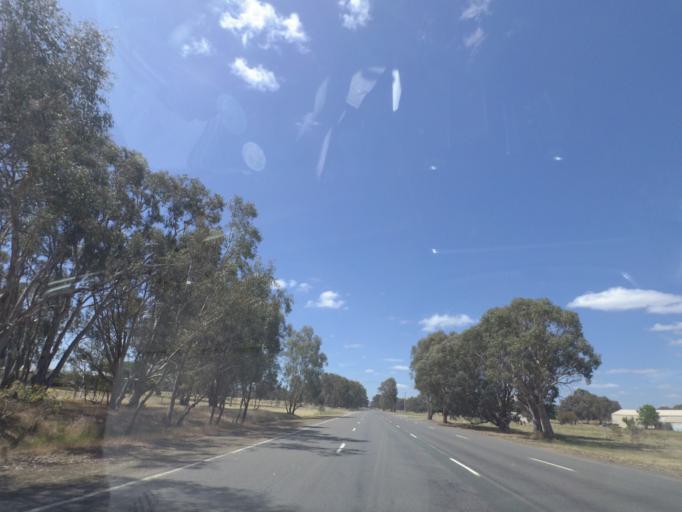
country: AU
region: Victoria
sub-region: Wangaratta
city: Wangaratta
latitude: -36.4291
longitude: 146.2549
